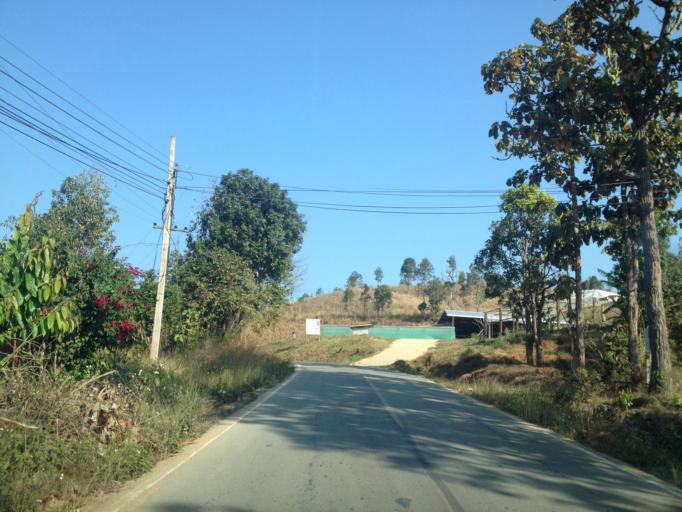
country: TH
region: Mae Hong Son
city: Ban Huai I Huak
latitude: 18.1065
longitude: 98.2202
